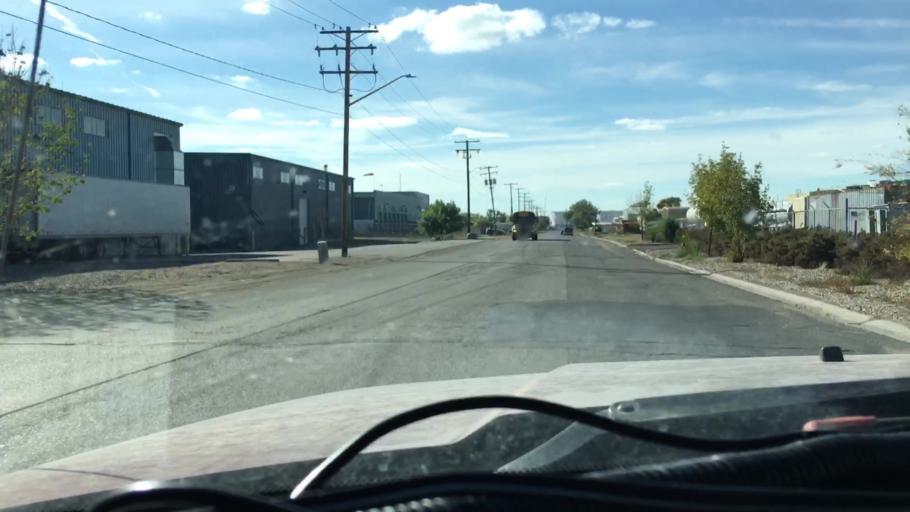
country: CA
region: Saskatchewan
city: Regina
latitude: 50.4786
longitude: -104.5649
